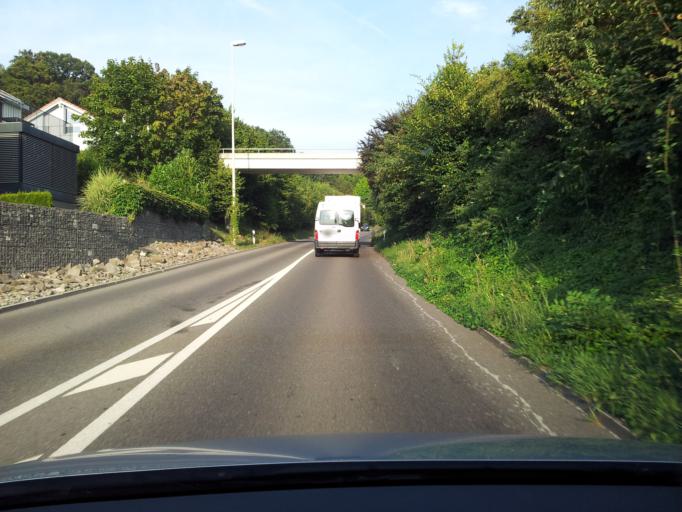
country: CH
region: Lucerne
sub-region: Sursee District
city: Sempach
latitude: 47.1379
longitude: 8.1931
